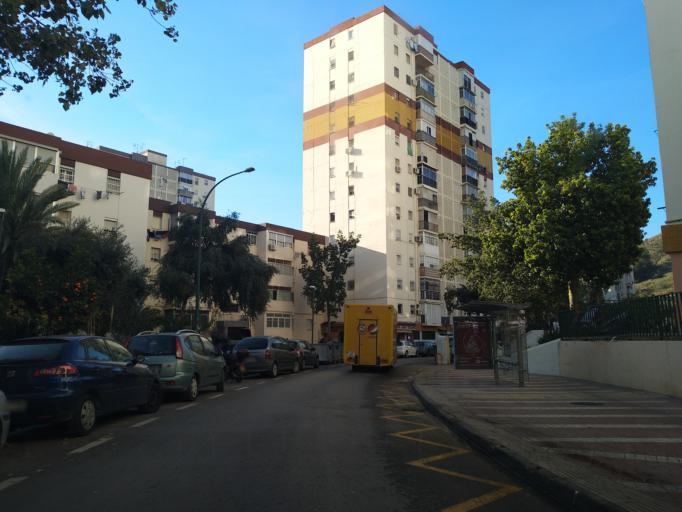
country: ES
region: Andalusia
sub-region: Provincia de Malaga
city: Malaga
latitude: 36.7406
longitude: -4.4320
